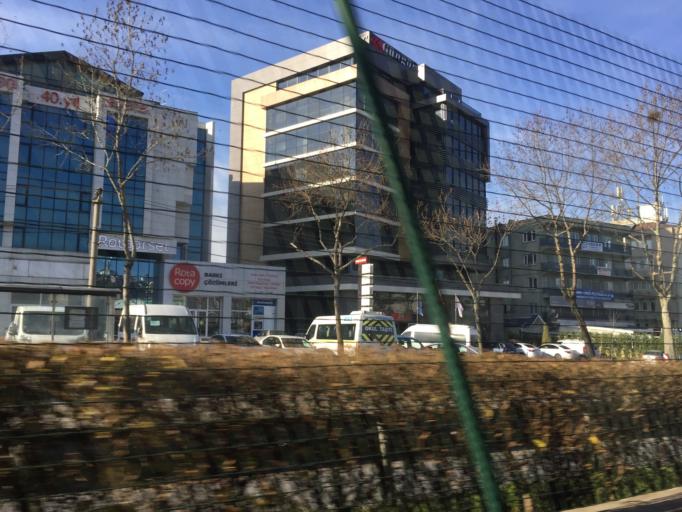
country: TR
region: Bursa
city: Niluefer
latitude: 40.2359
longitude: 28.9768
